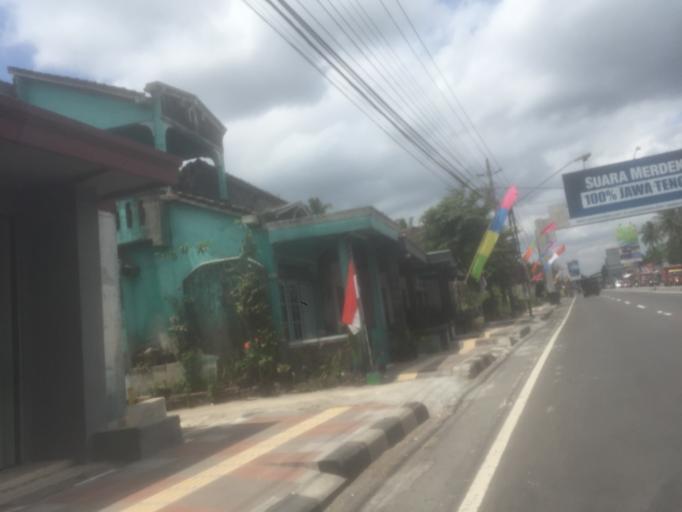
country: ID
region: Central Java
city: Muntilan
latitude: -7.6385
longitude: 110.3215
